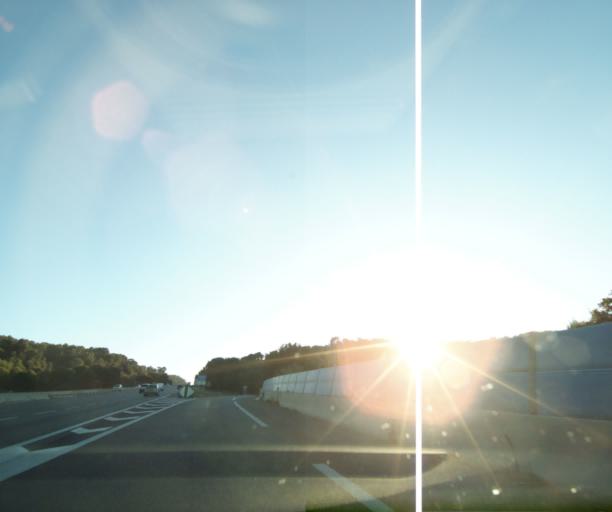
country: FR
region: Provence-Alpes-Cote d'Azur
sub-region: Departement des Bouches-du-Rhone
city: Roquefort-la-Bedoule
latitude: 43.2442
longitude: 5.5950
